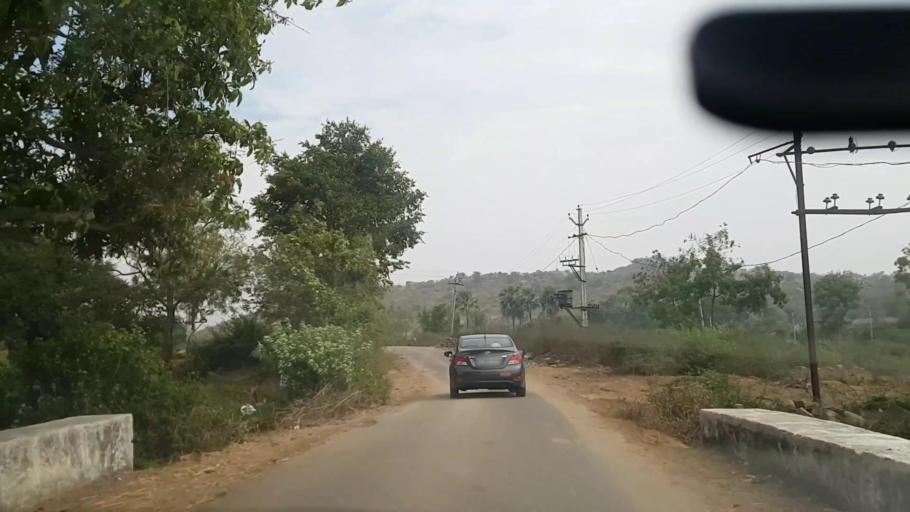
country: IN
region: Telangana
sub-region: Rangareddi
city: Lal Bahadur Nagar
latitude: 17.1746
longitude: 78.7770
